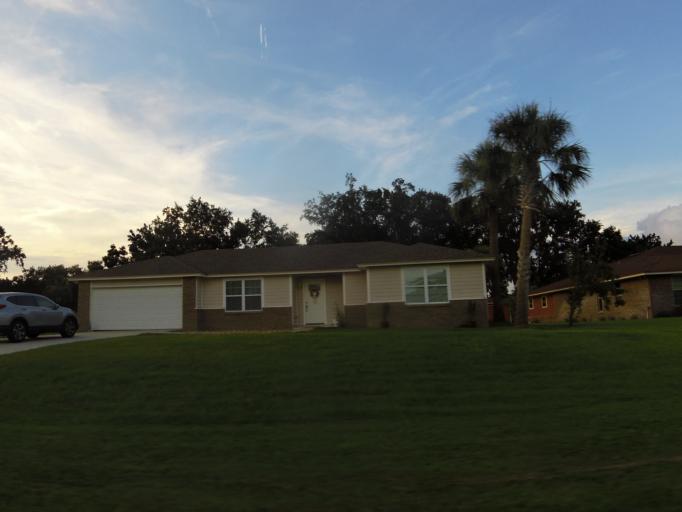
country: US
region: Florida
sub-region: Duval County
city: Atlantic Beach
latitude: 30.3936
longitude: -81.5006
